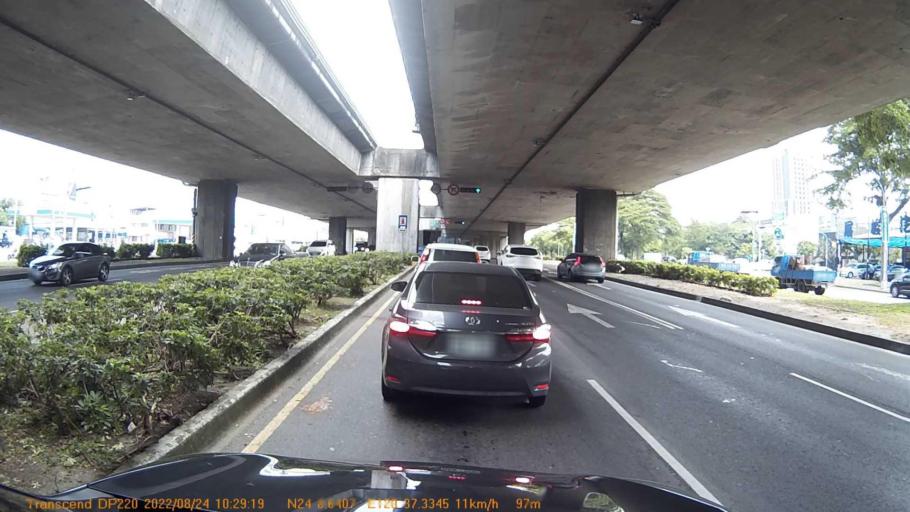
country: TW
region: Taiwan
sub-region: Taichung City
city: Taichung
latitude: 24.1442
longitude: 120.6224
